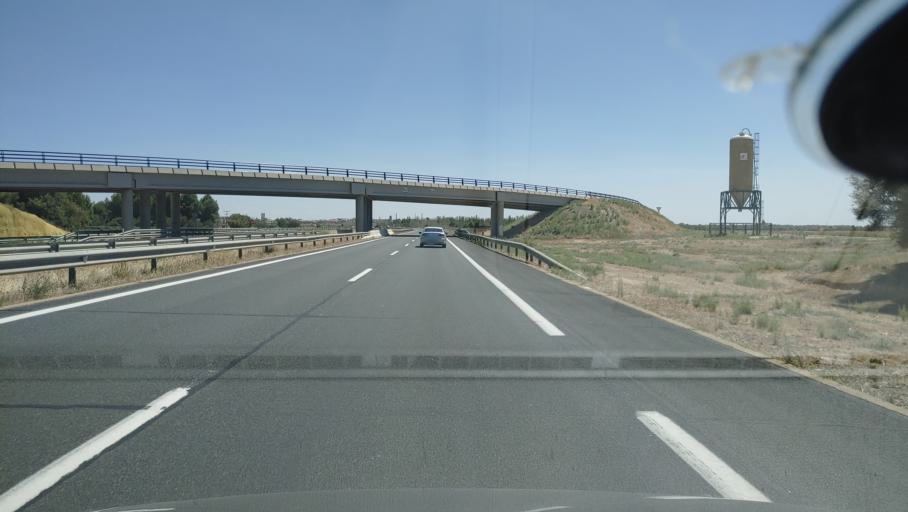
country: ES
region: Castille-La Mancha
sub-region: Provincia de Ciudad Real
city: Villarta de San Juan
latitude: 39.2527
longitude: -3.4332
